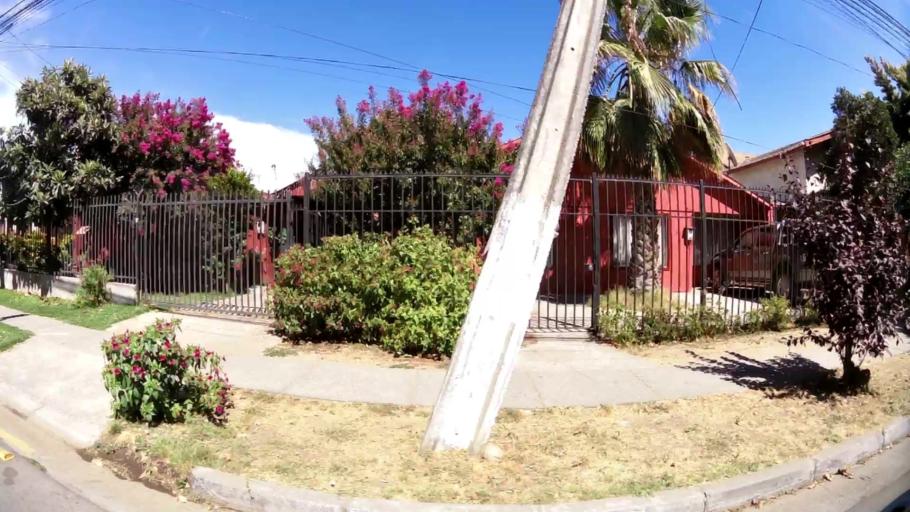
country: CL
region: O'Higgins
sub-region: Provincia de Cachapoal
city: Graneros
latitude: -33.9732
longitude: -70.7093
